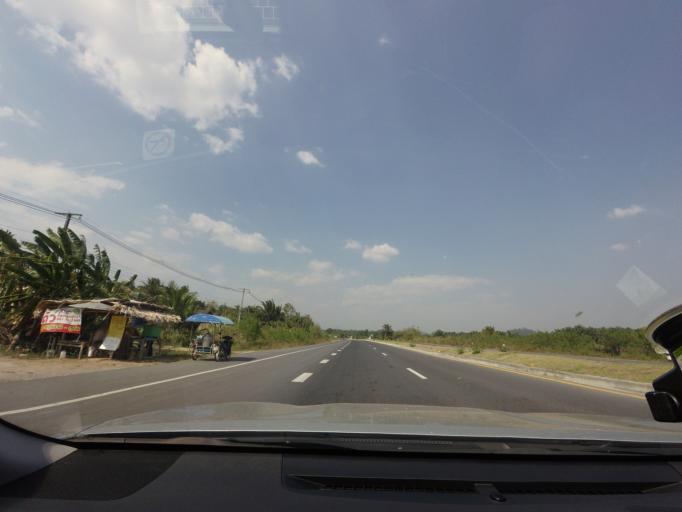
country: TH
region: Phangnga
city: Thap Put
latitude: 8.5481
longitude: 98.7290
